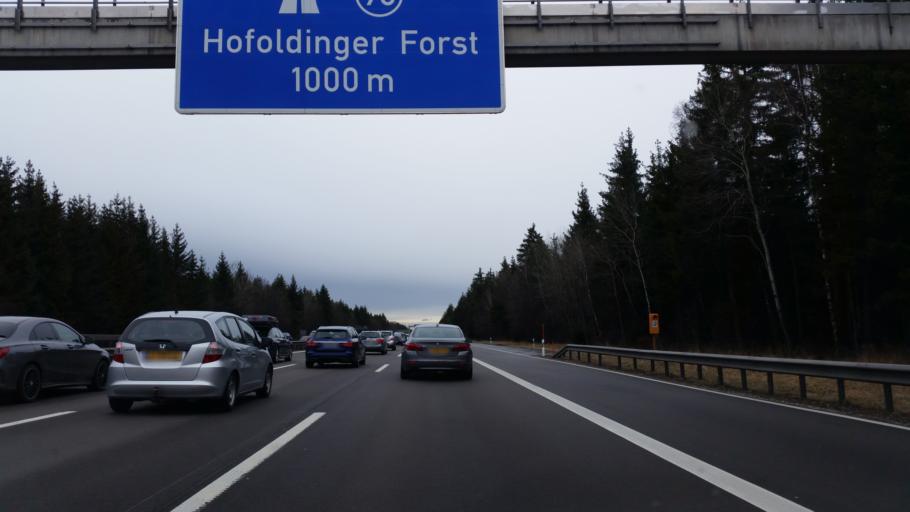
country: DE
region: Bavaria
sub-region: Upper Bavaria
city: Sauerlach
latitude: 47.9673
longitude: 11.6876
